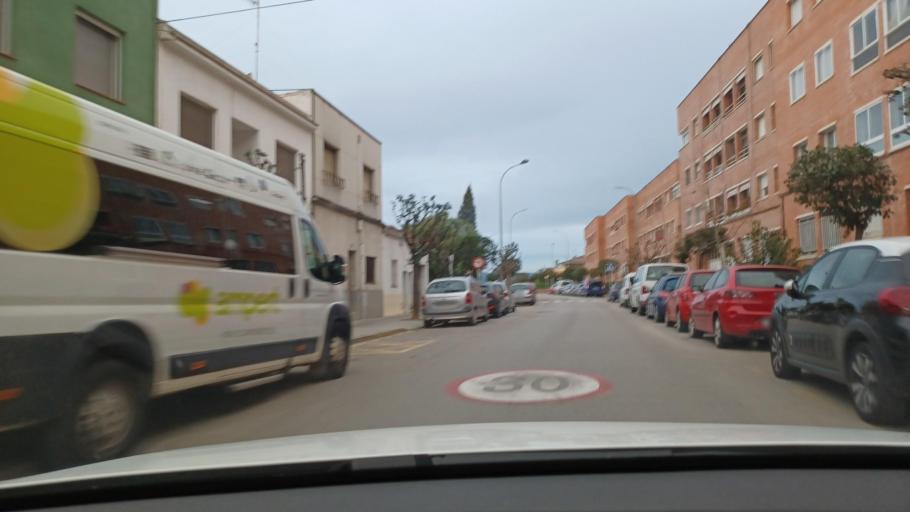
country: ES
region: Catalonia
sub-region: Provincia de Barcelona
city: Vilafranca del Penedes
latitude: 41.3434
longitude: 1.6921
